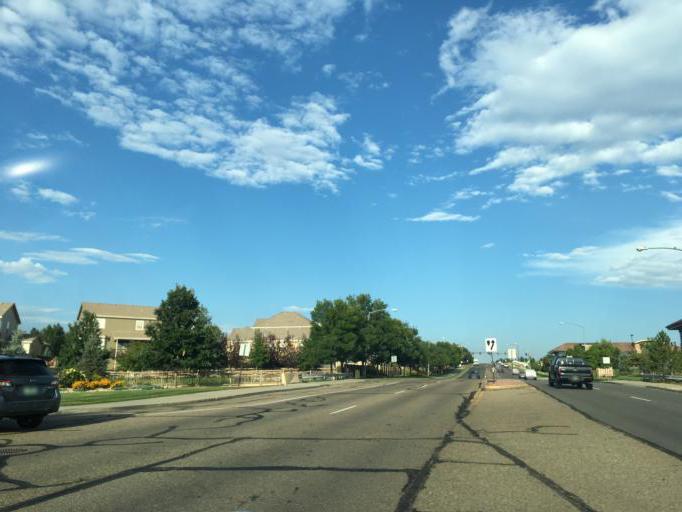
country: US
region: Colorado
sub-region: Adams County
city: Northglenn
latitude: 39.9429
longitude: -104.9550
